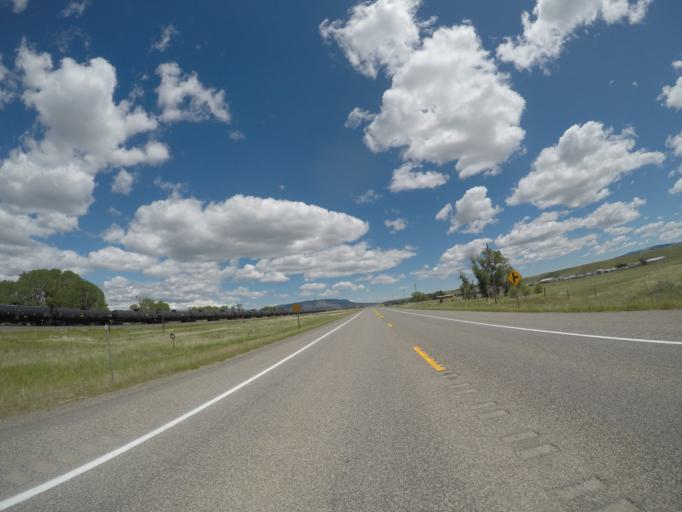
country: US
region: Montana
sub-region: Park County
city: Livingston
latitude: 45.6806
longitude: -110.5222
